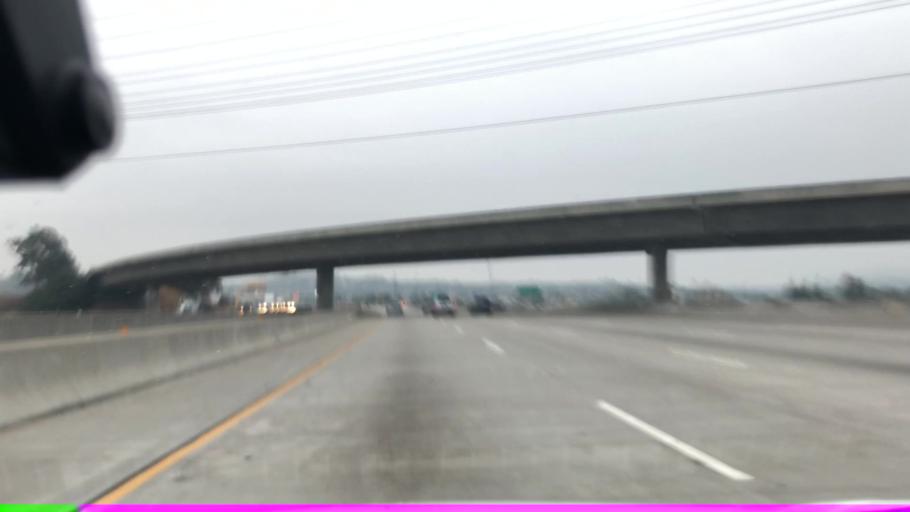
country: US
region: California
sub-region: San Diego County
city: Escondido
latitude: 33.1272
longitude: -117.1050
